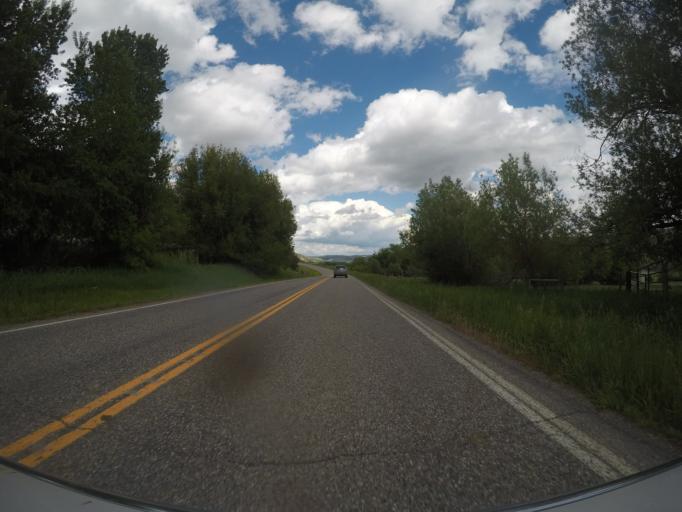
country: US
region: Montana
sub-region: Sweet Grass County
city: Big Timber
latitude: 45.6855
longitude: -110.0795
